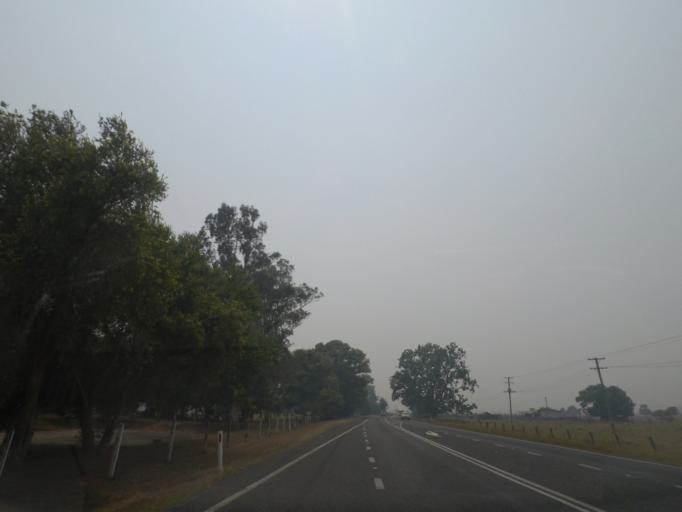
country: AU
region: New South Wales
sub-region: Clarence Valley
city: Maclean
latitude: -29.5648
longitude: 153.1040
